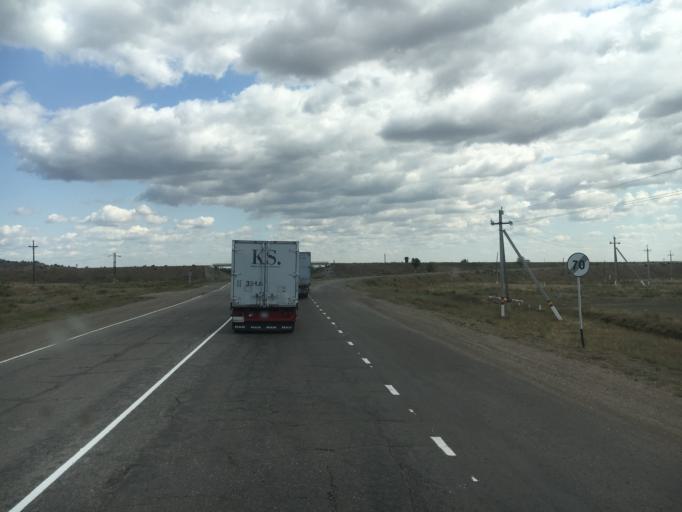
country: KZ
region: Qostanay
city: Rudnyy
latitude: 52.9816
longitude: 63.2216
